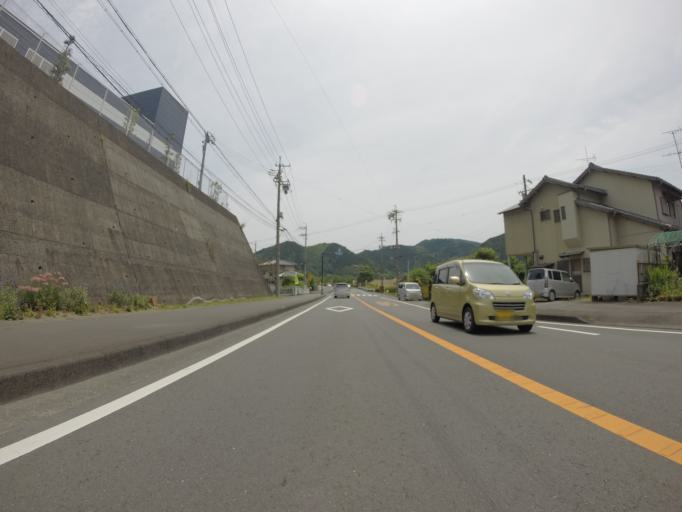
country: JP
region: Shizuoka
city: Shizuoka-shi
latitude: 34.9847
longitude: 138.3145
